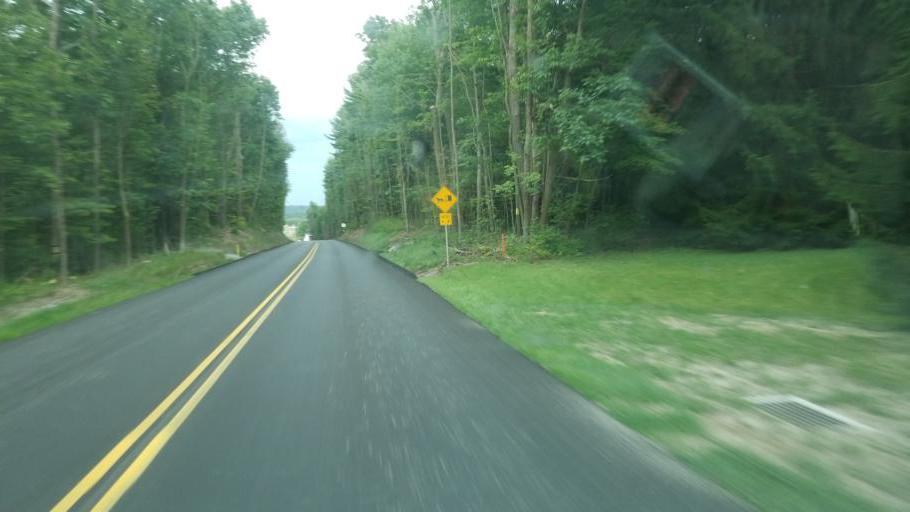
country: US
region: Pennsylvania
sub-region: Clarion County
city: Knox
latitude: 41.2479
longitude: -79.5438
